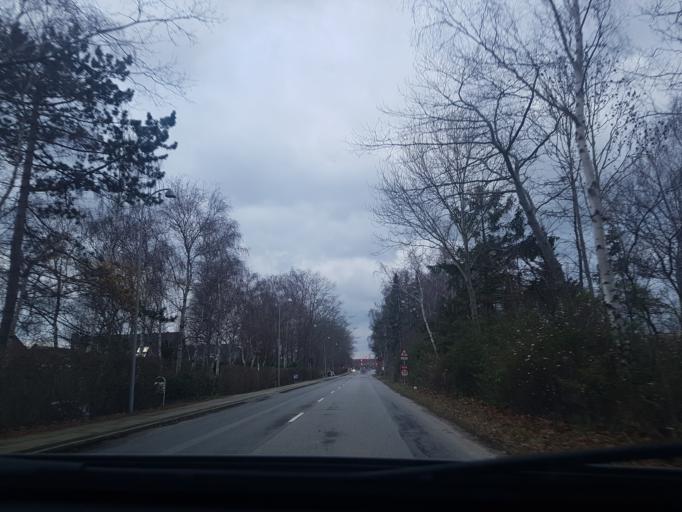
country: DK
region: Capital Region
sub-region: Ishoj Kommune
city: Ishoj
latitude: 55.6106
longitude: 12.3702
